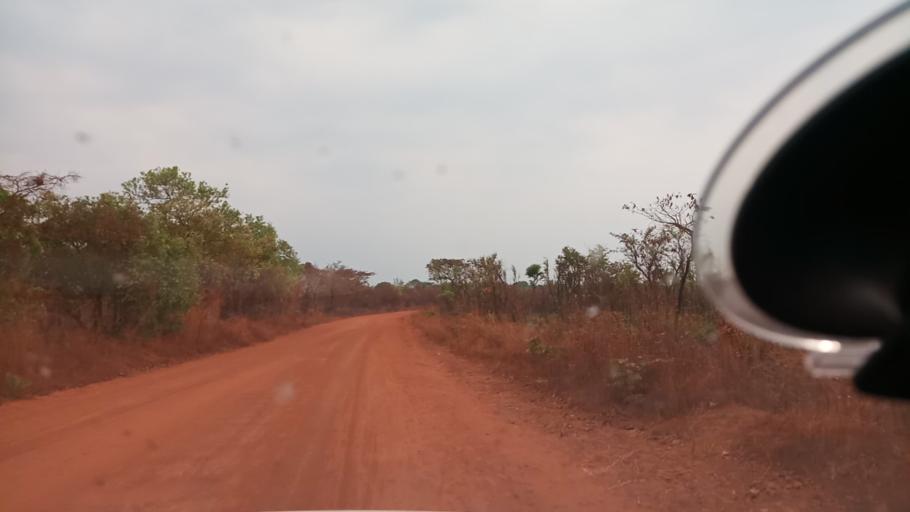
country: ZM
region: Luapula
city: Nchelenge
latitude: -9.1722
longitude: 28.2813
